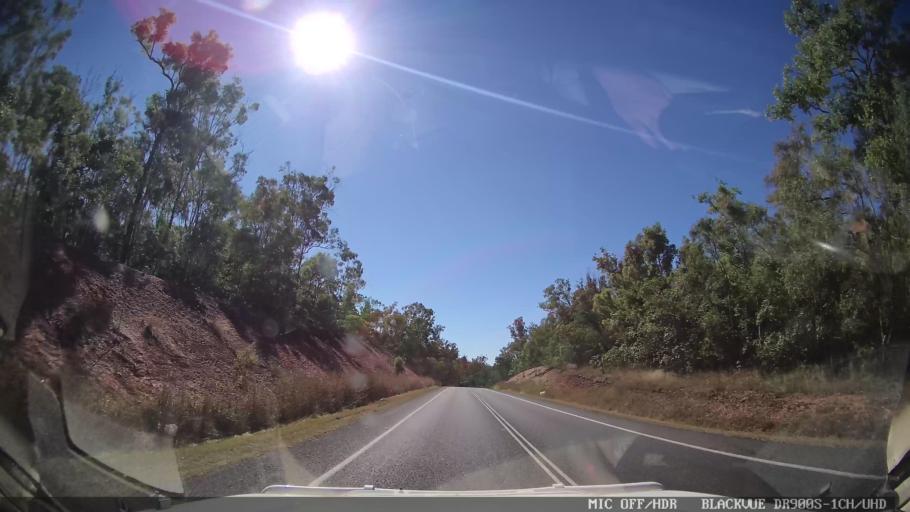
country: AU
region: Queensland
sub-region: Gladstone
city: Toolooa
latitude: -23.9651
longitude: 151.2175
